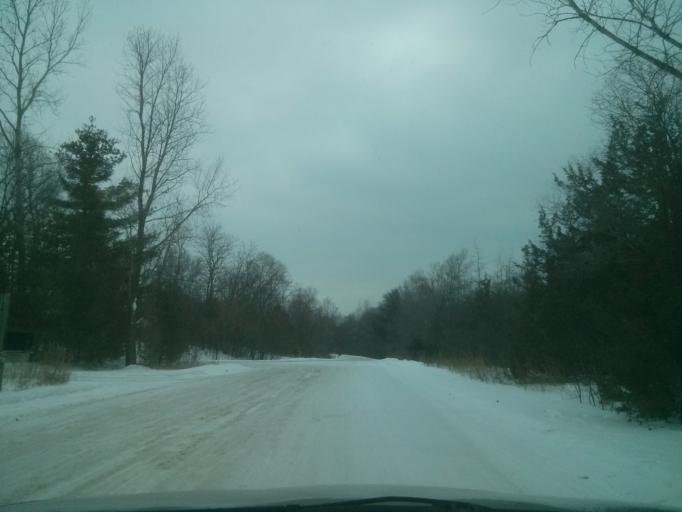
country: US
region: Minnesota
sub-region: Washington County
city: Lakeland
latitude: 44.9392
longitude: -92.7733
